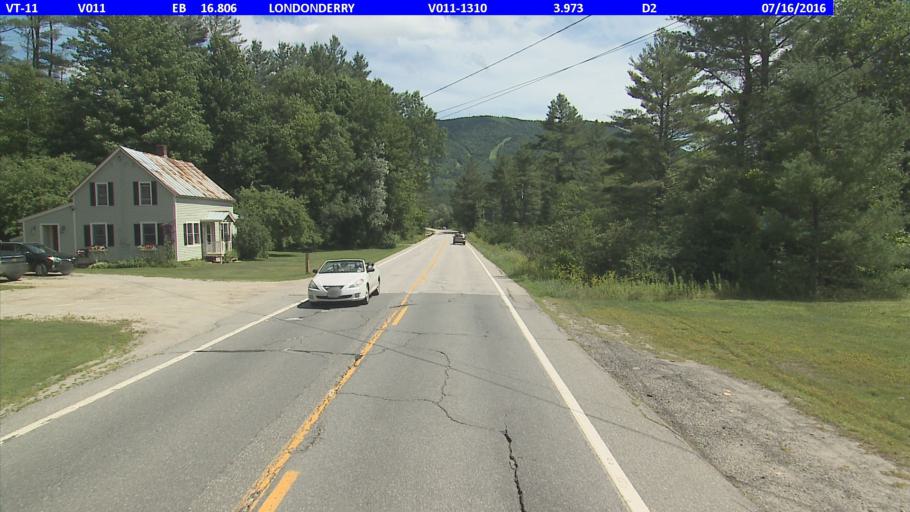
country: US
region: Vermont
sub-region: Windsor County
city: Chester
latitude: 43.2116
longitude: -72.7862
